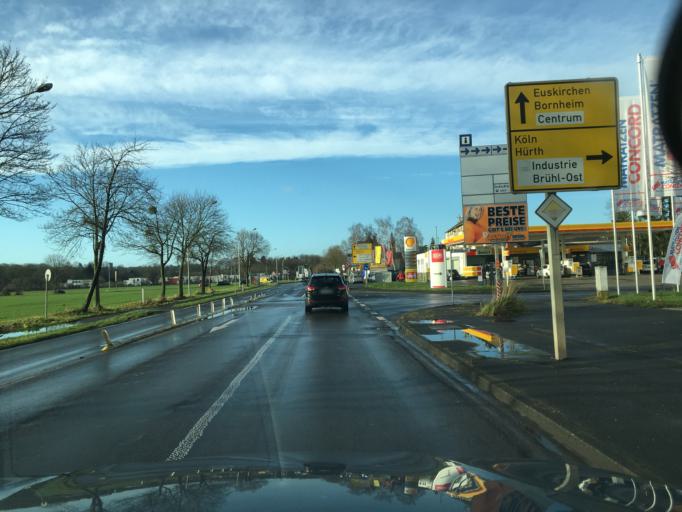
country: DE
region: North Rhine-Westphalia
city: Bruhl
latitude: 50.8295
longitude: 6.9256
